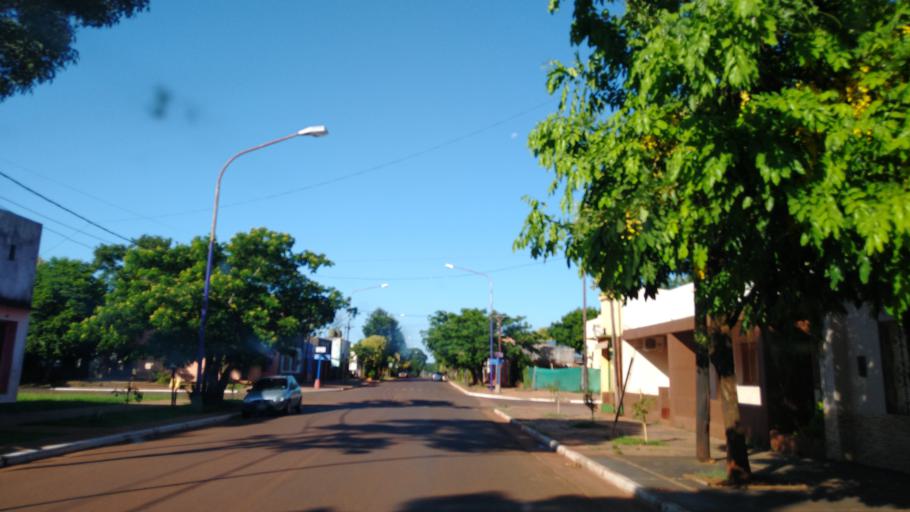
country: AR
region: Misiones
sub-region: Departamento de San Ignacio
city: San Ignacio
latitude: -27.2547
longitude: -55.5356
